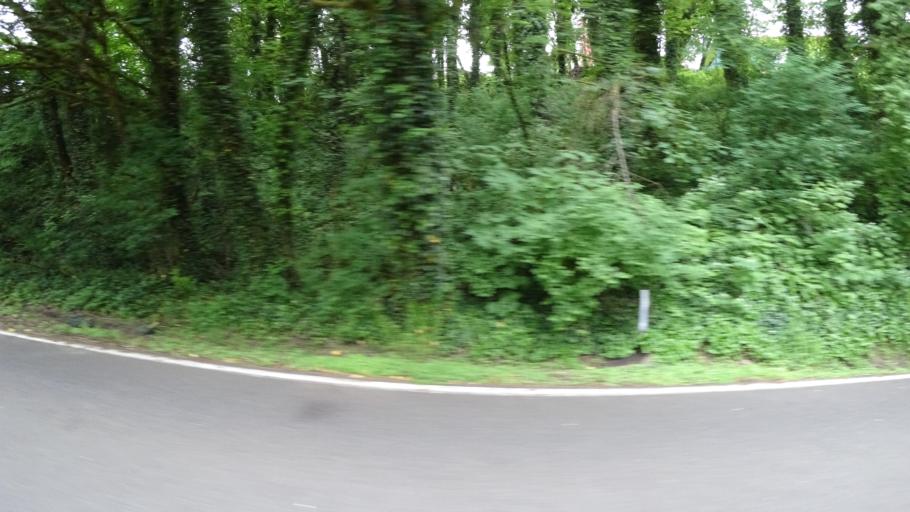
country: US
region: Oregon
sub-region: Multnomah County
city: Portland
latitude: 45.4896
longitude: -122.6951
